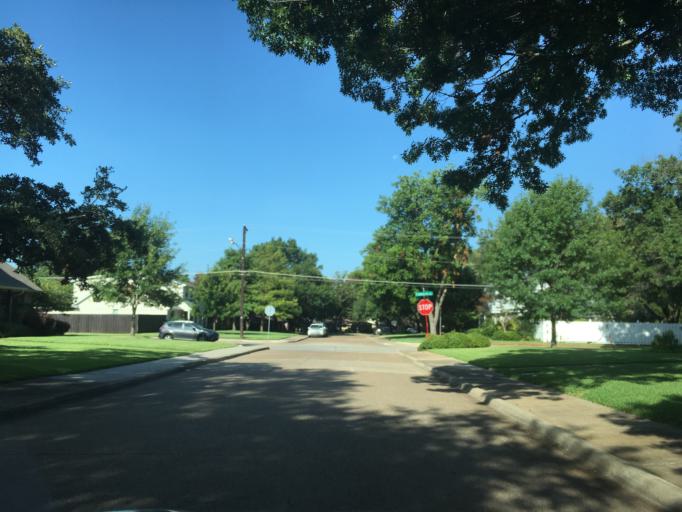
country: US
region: Texas
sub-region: Dallas County
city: Richardson
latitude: 32.8825
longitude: -96.7243
